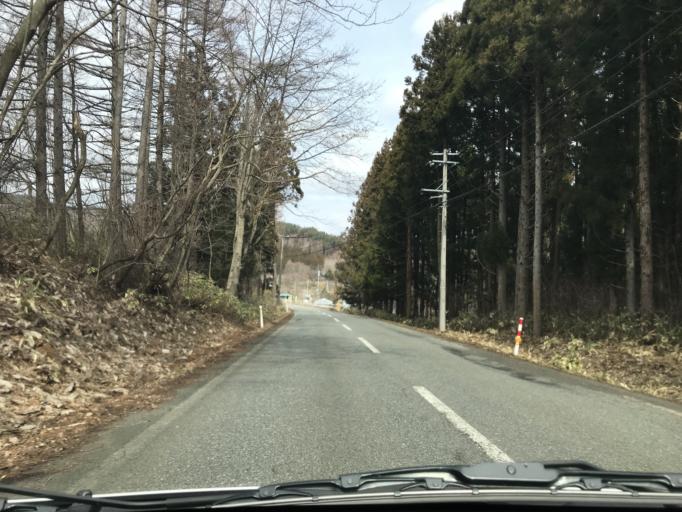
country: JP
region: Iwate
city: Kitakami
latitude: 39.2588
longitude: 141.3170
